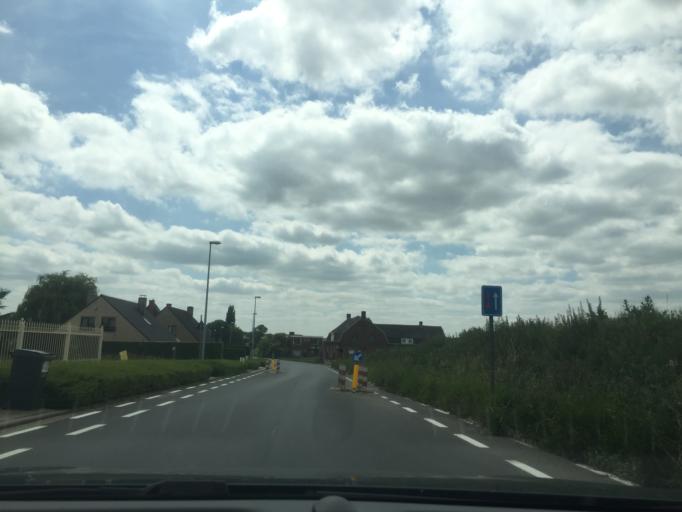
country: BE
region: Flanders
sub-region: Provincie West-Vlaanderen
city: Zwevegem
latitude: 50.7564
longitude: 3.3600
